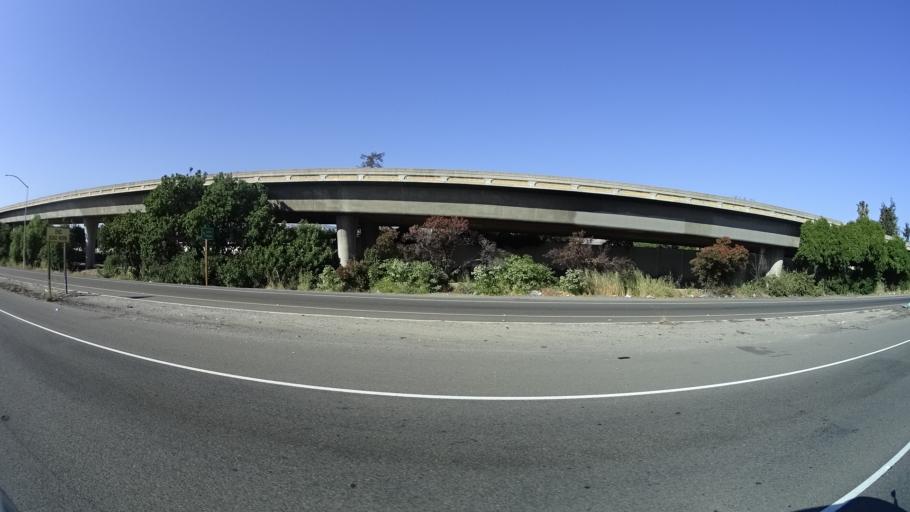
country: US
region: California
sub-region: Santa Clara County
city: Alum Rock
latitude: 37.3339
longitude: -121.8462
